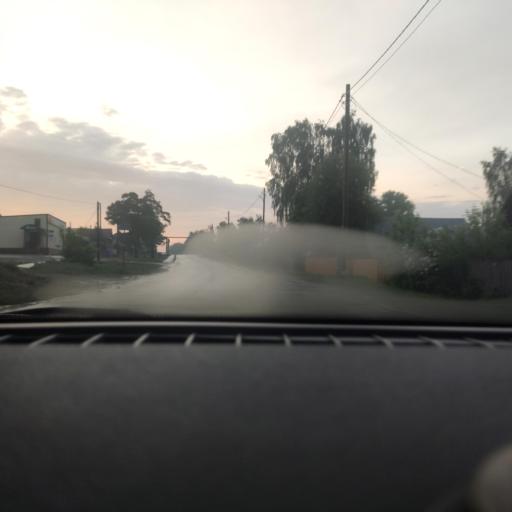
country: RU
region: Perm
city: Nytva
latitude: 57.8960
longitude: 55.4852
